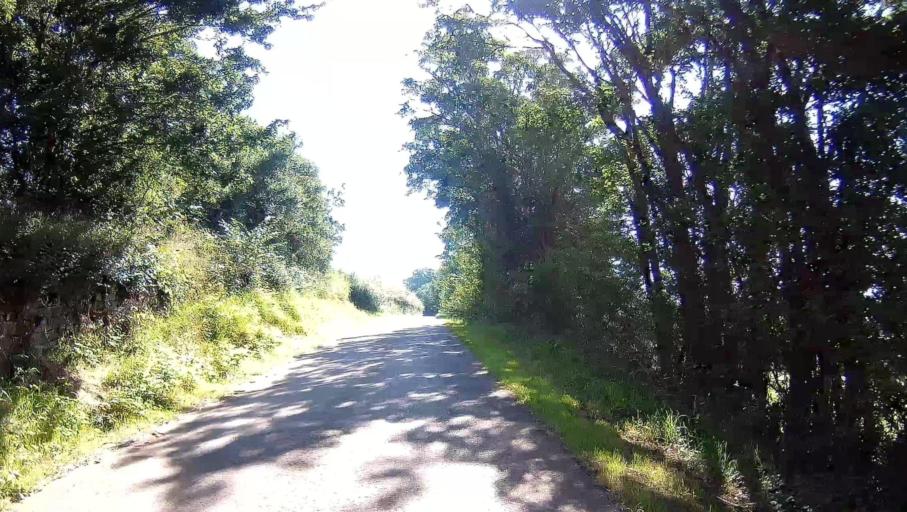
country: FR
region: Bourgogne
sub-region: Departement de Saone-et-Loire
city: Saint-Leger-sur-Dheune
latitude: 46.8676
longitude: 4.6295
